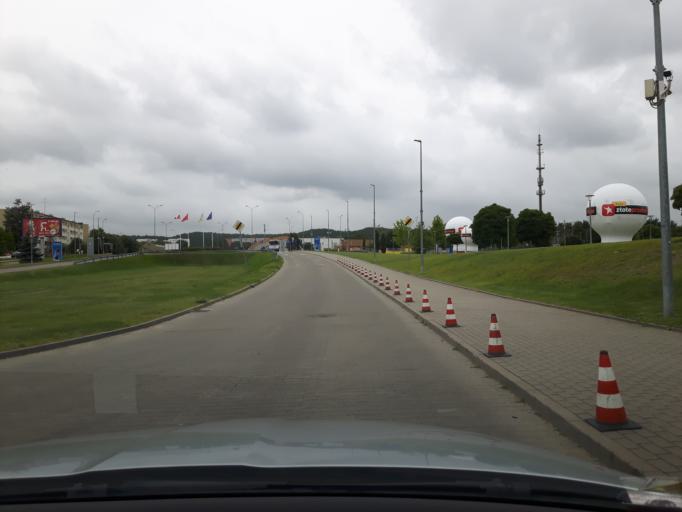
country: PL
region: Pomeranian Voivodeship
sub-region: Sopot
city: Sopot
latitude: 54.4257
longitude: 18.5795
